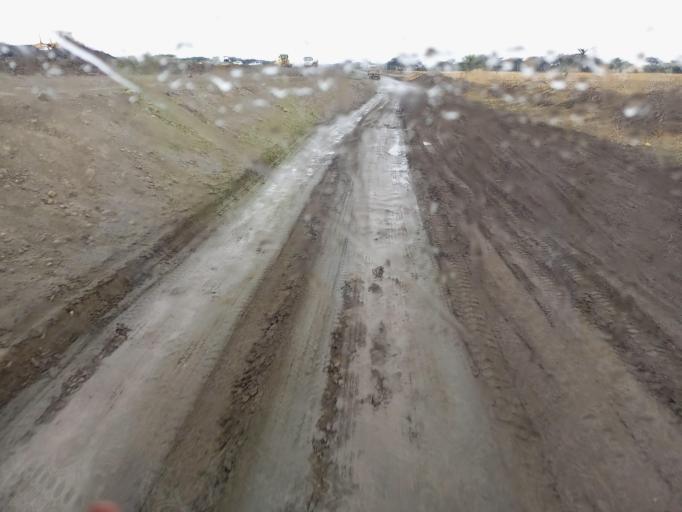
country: ET
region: Oromiya
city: Ziway
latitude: 7.7565
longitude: 38.6112
